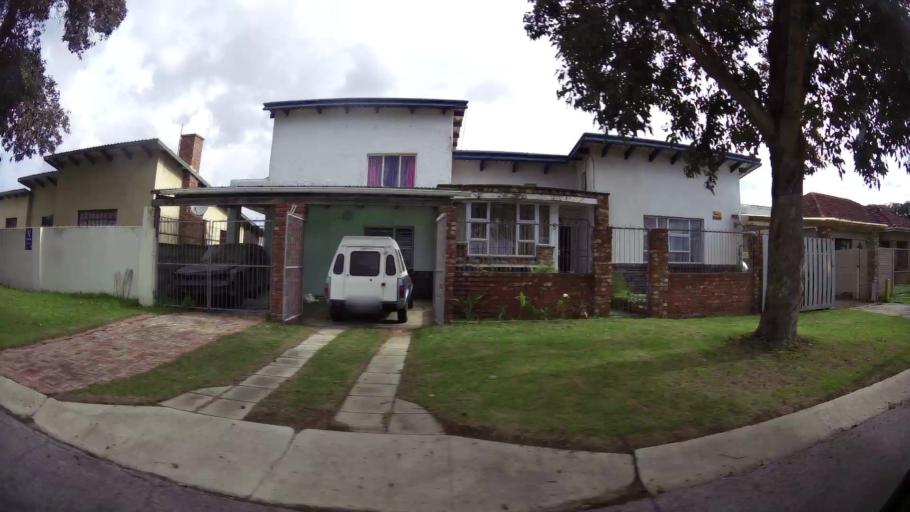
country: ZA
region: Eastern Cape
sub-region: Nelson Mandela Bay Metropolitan Municipality
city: Port Elizabeth
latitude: -33.9405
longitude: 25.5550
